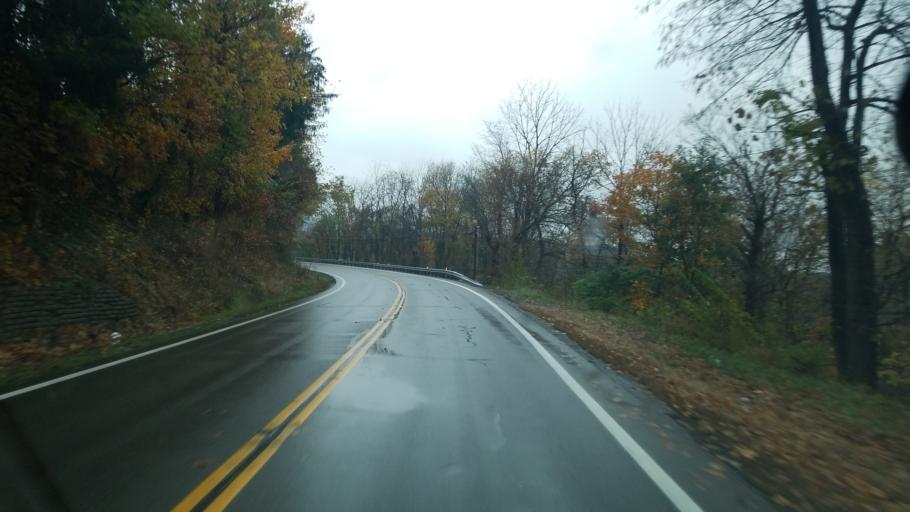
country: US
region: Ohio
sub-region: Coshocton County
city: Coshocton
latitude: 40.2991
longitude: -81.8696
